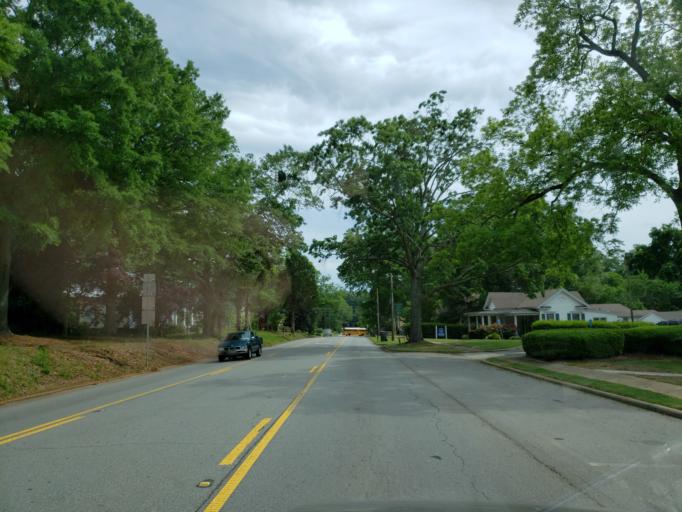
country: US
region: Georgia
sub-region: Monroe County
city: Forsyth
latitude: 33.0332
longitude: -83.9385
